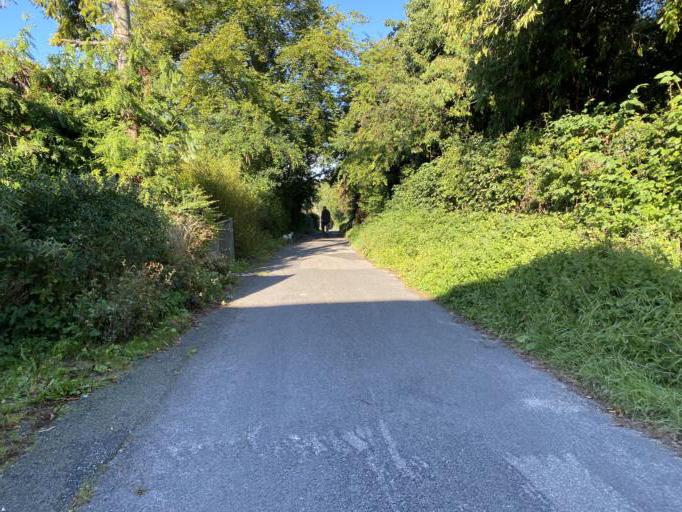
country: DK
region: Zealand
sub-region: Guldborgsund Kommune
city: Sakskobing
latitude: 54.9801
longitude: 11.5344
